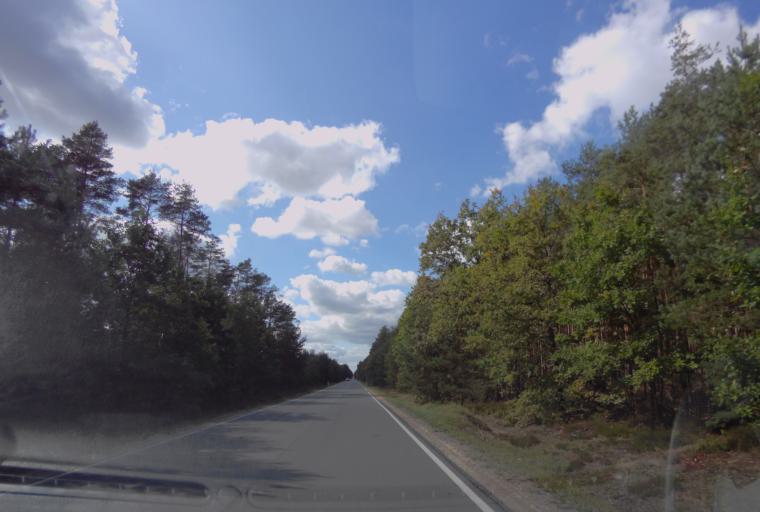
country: PL
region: Subcarpathian Voivodeship
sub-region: Powiat tarnobrzeski
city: Nowa Deba
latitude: 50.4153
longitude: 21.8498
